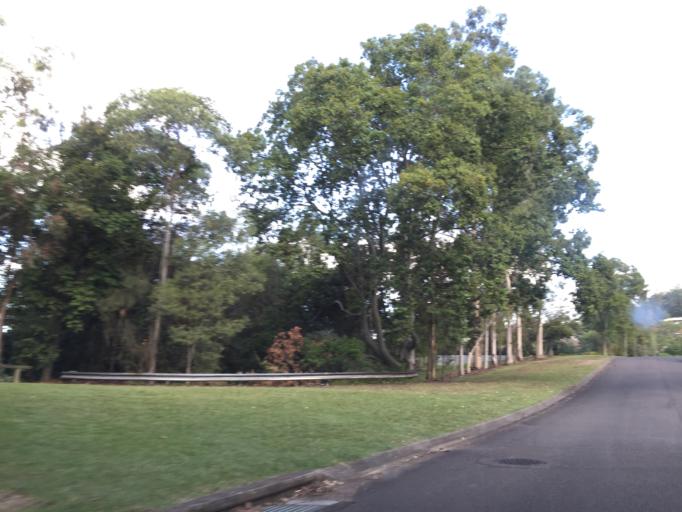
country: AU
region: Queensland
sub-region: Moreton Bay
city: Ferny Hills
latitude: -27.4375
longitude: 152.9315
